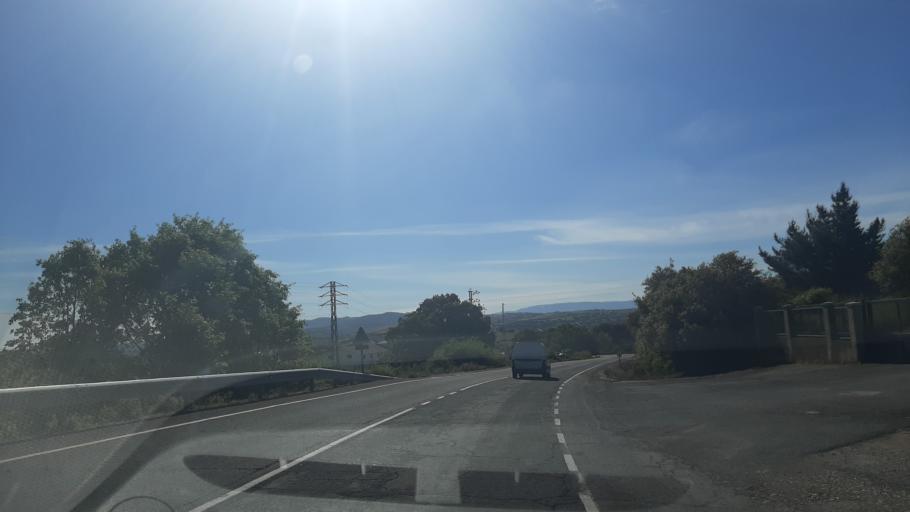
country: ES
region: Castille and Leon
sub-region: Provincia de Salamanca
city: Guijuelo
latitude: 40.5572
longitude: -5.6522
